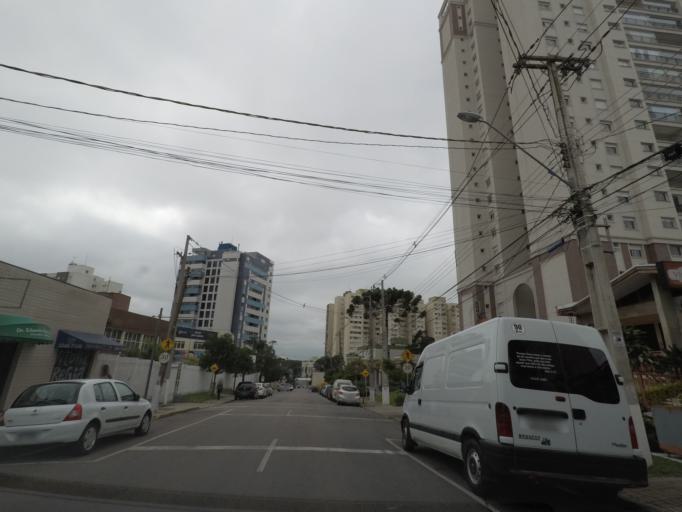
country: BR
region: Parana
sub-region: Curitiba
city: Curitiba
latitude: -25.4713
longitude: -49.2934
